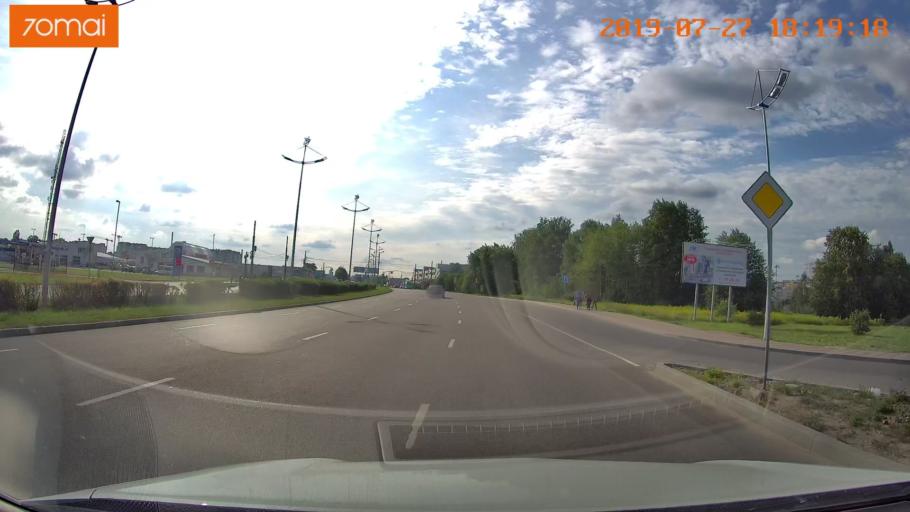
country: RU
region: Kaliningrad
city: Bol'shoe Isakovo
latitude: 54.7066
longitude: 20.5860
